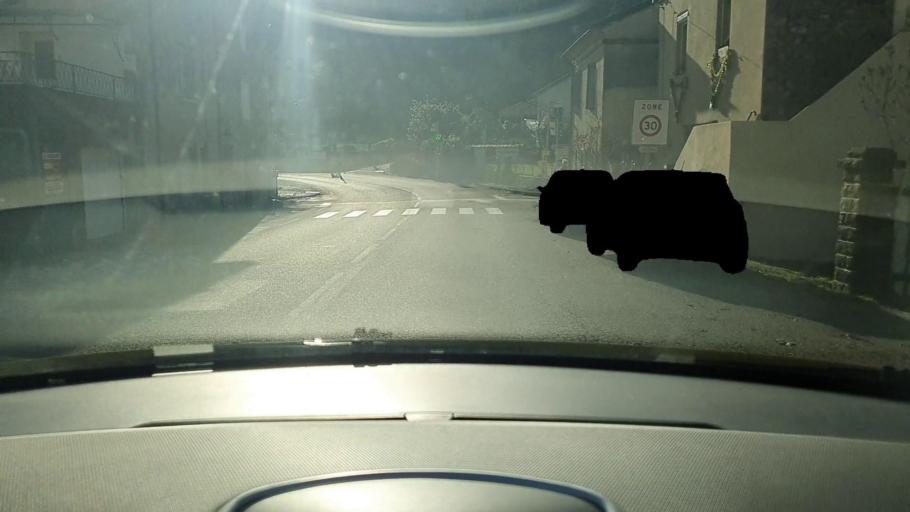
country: FR
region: Languedoc-Roussillon
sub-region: Departement du Gard
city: Branoux-les-Taillades
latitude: 44.3063
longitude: 3.9705
